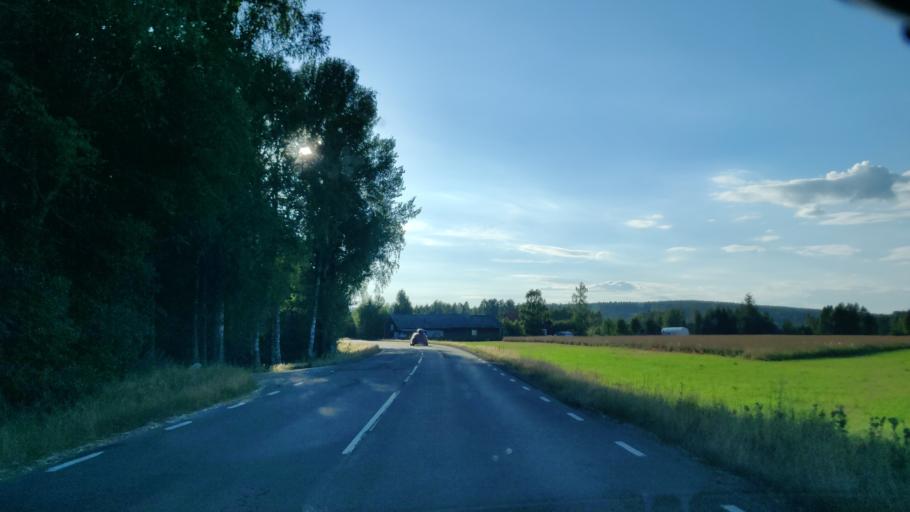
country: SE
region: Vaermland
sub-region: Hagfors Kommun
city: Ekshaerad
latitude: 60.1780
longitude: 13.5174
